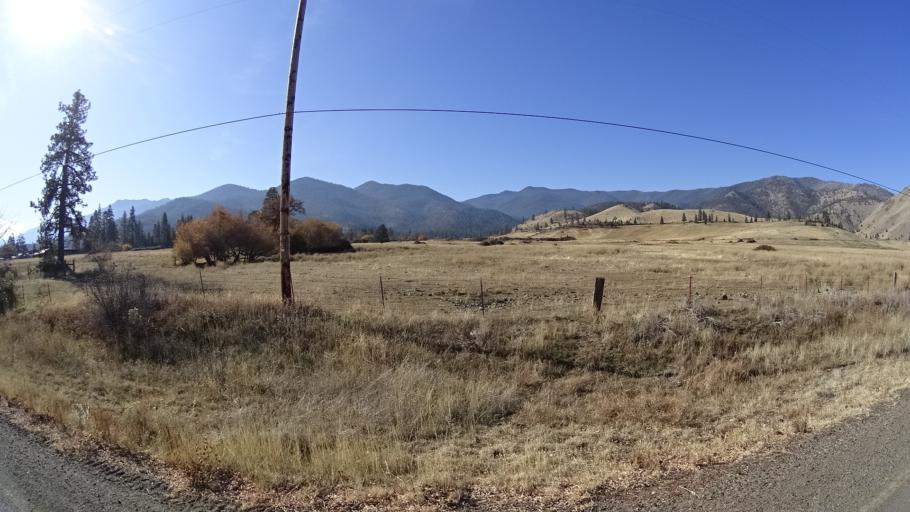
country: US
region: California
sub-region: Siskiyou County
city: Weed
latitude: 41.4496
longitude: -122.4527
